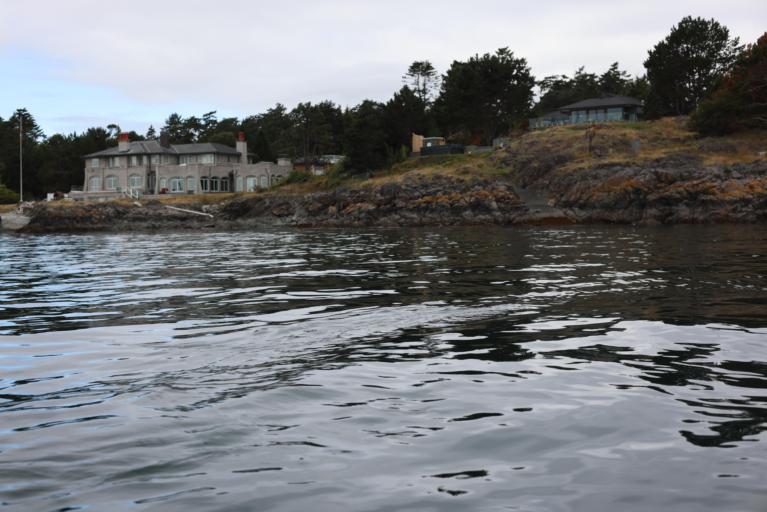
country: CA
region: British Columbia
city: Oak Bay
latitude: 48.4525
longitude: -123.2641
